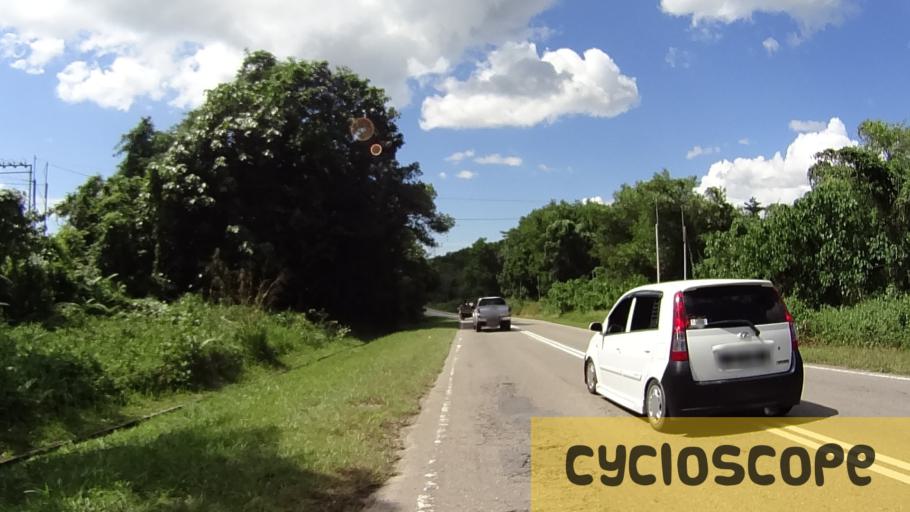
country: MY
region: Sabah
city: Beaufort
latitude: 5.1258
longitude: 115.6226
